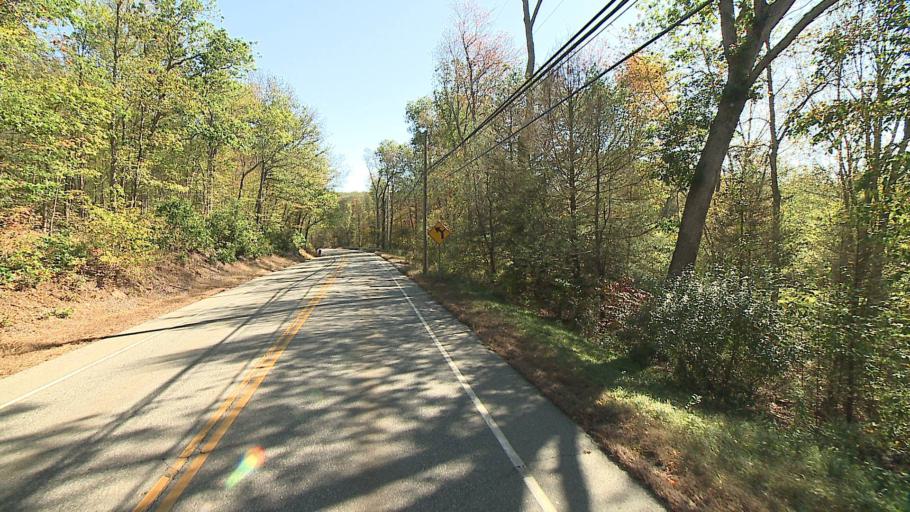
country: US
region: Connecticut
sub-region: Tolland County
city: Hebron
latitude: 41.6471
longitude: -72.4049
